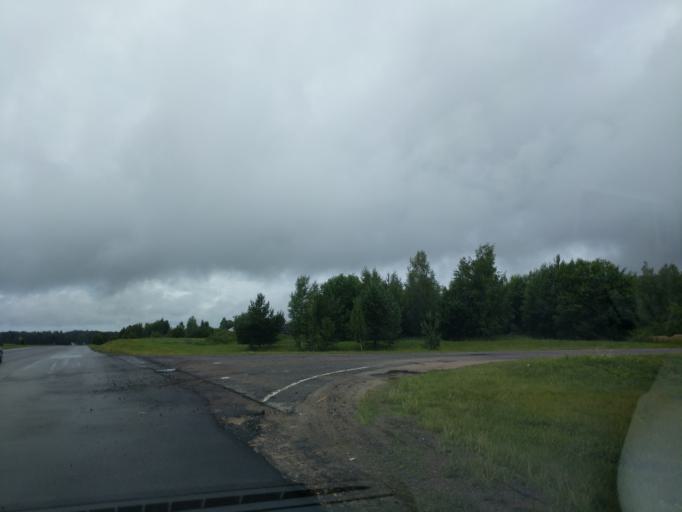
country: BY
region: Minsk
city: Syomkava
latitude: 54.2582
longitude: 27.4945
